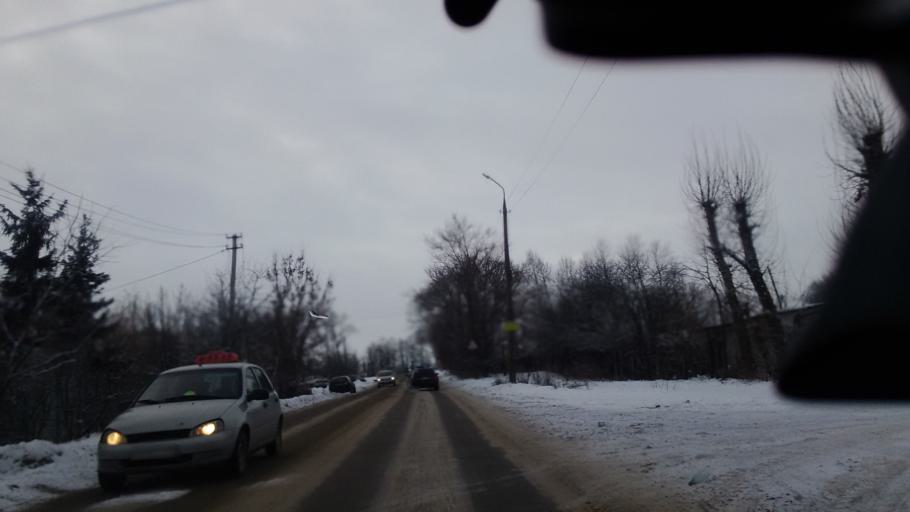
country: RU
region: Tula
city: Bogoroditsk
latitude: 53.7650
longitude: 38.1090
